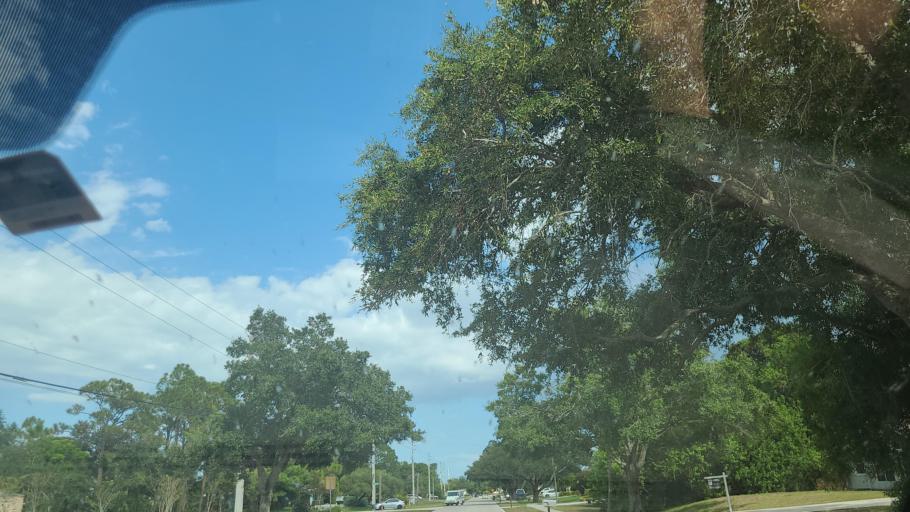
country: US
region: Florida
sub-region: Saint Lucie County
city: Port Saint Lucie
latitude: 27.2567
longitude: -80.3676
